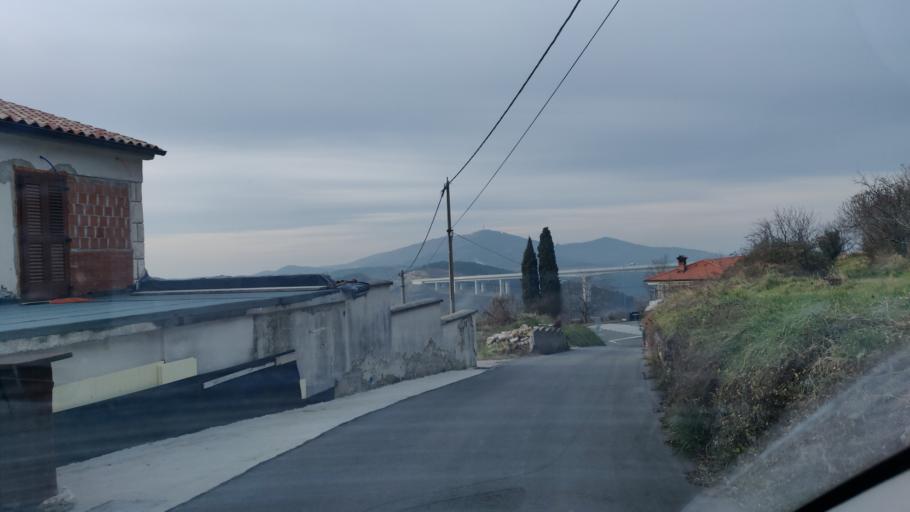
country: SI
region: Koper-Capodistria
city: Sv. Anton
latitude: 45.5499
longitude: 13.8781
